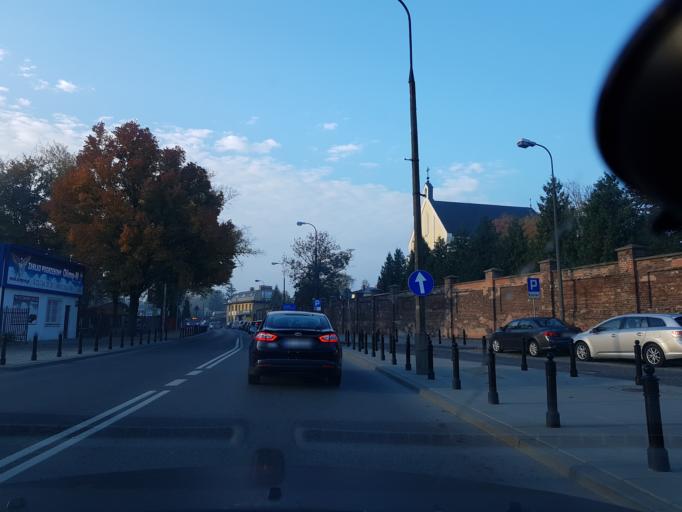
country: PL
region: Masovian Voivodeship
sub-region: Warszawa
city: Targowek
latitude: 52.2775
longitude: 21.0436
